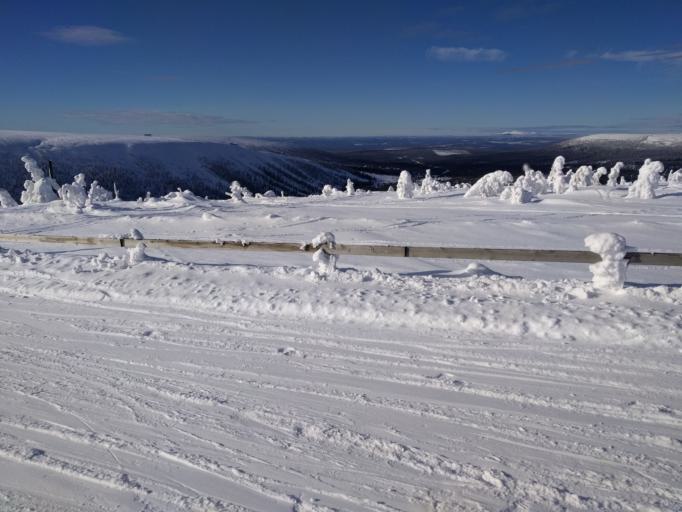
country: NO
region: Hedmark
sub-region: Trysil
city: Innbygda
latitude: 61.1733
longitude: 13.0163
